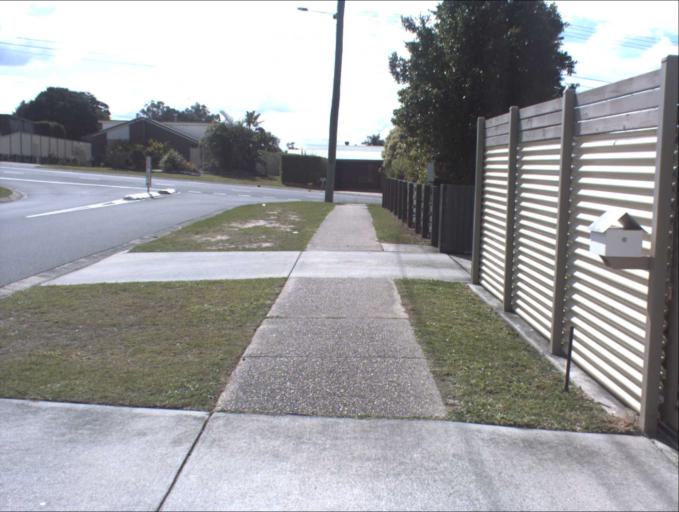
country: AU
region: Queensland
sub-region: Logan
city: Park Ridge South
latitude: -27.6741
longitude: 153.0375
